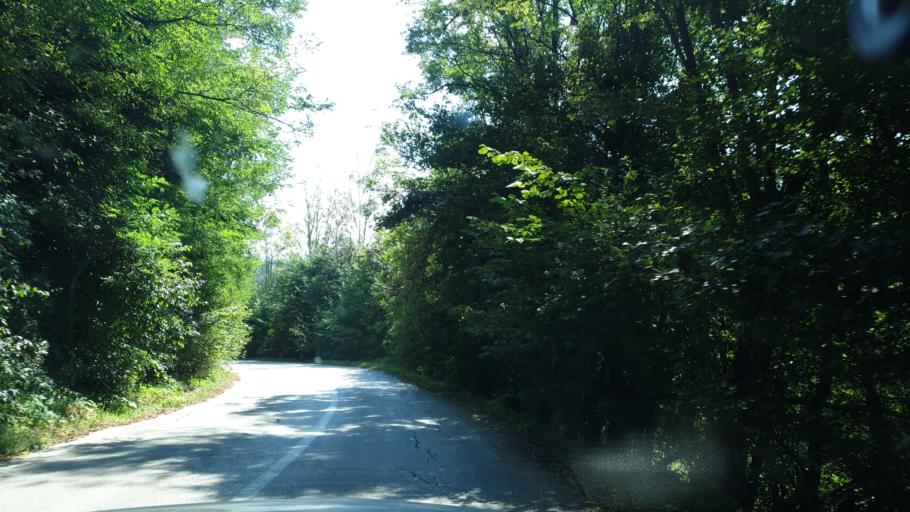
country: RS
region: Central Serbia
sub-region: Zlatiborski Okrug
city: Cajetina
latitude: 43.6722
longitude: 19.8272
